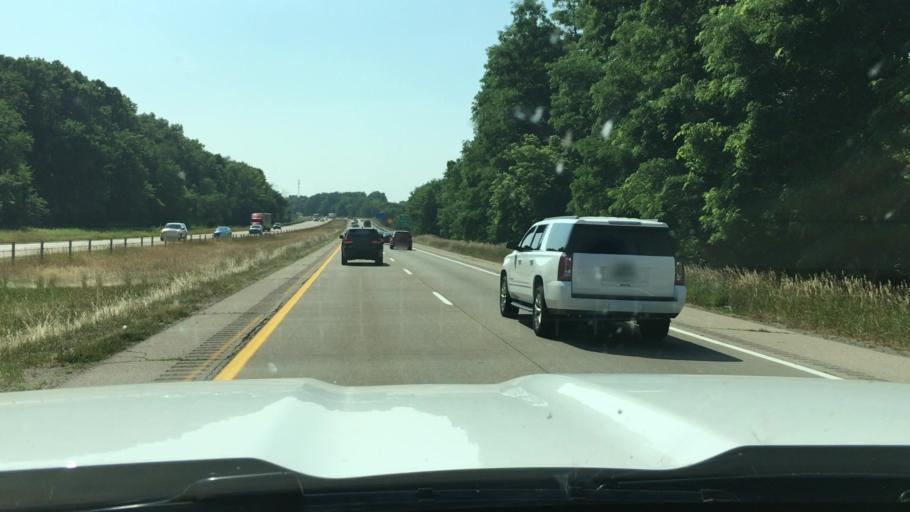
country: US
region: Michigan
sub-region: Ionia County
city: Portland
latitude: 42.8607
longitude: -84.8958
